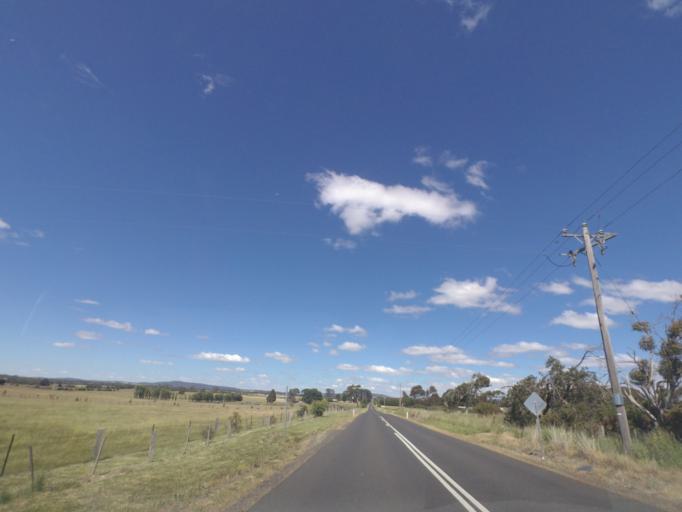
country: AU
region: Victoria
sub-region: Mount Alexander
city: Castlemaine
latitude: -37.2869
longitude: 144.4491
